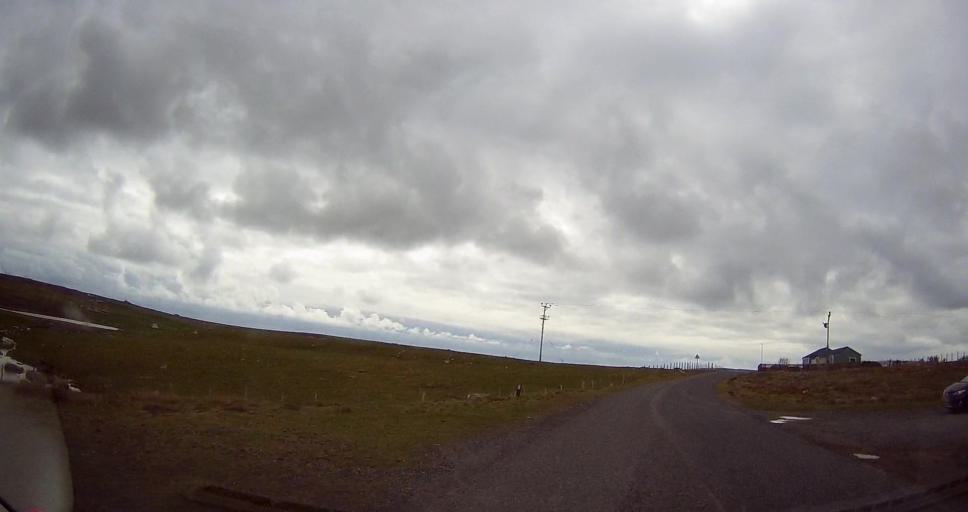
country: GB
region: Scotland
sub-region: Shetland Islands
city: Shetland
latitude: 60.6954
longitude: -0.9235
